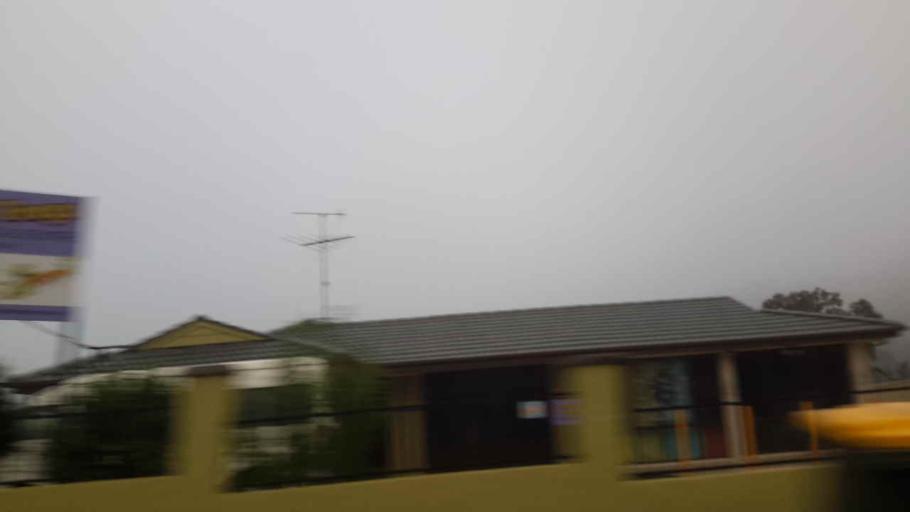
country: AU
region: New South Wales
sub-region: Wollondilly
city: Douglas Park
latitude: -34.1826
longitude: 150.7107
